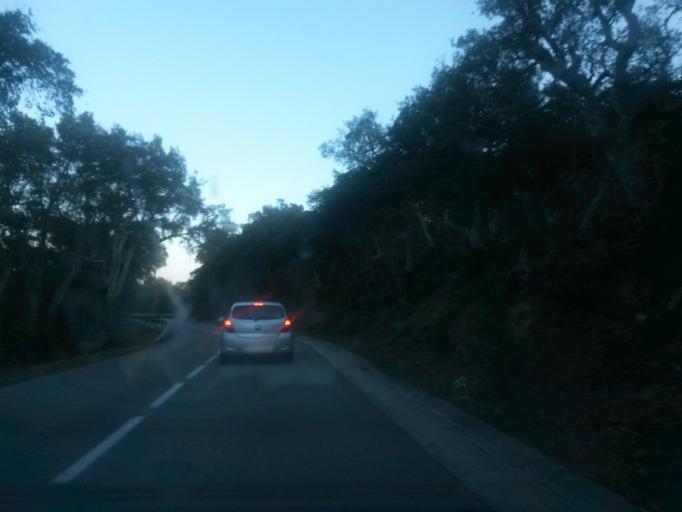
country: ES
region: Catalonia
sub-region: Provincia de Girona
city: Darnius
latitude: 42.3718
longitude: 2.8093
